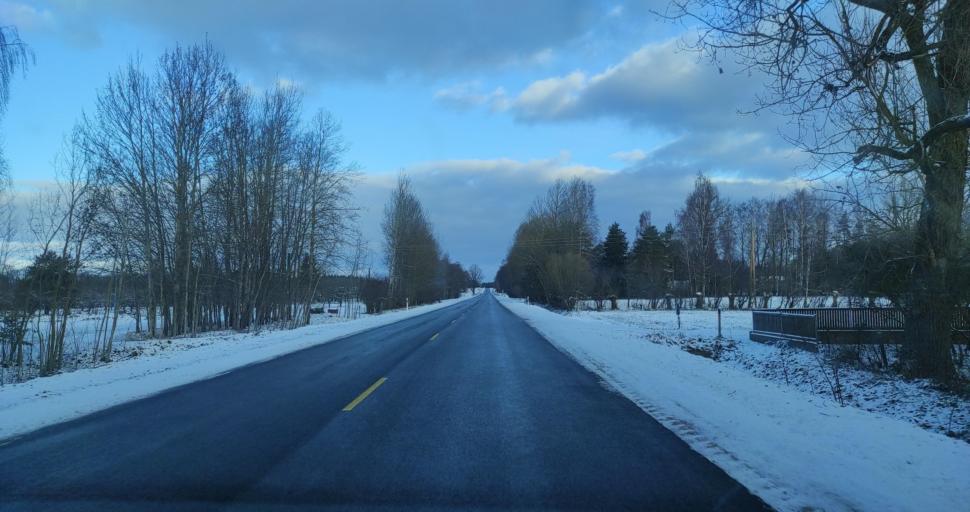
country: LV
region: Skrunda
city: Skrunda
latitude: 56.7102
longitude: 22.0132
